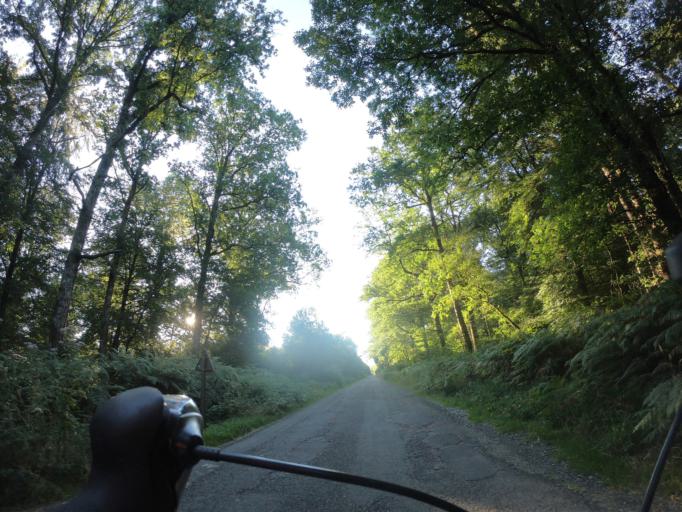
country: FR
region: Lower Normandy
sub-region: Departement de l'Orne
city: Magny-le-Desert
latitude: 48.5381
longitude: -0.3252
